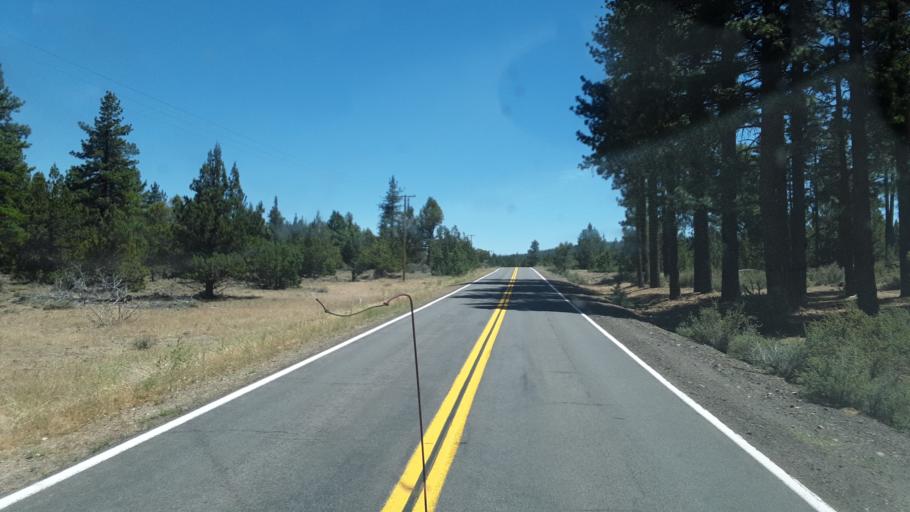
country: US
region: California
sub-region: Lassen County
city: Susanville
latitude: 40.5073
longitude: -120.5715
